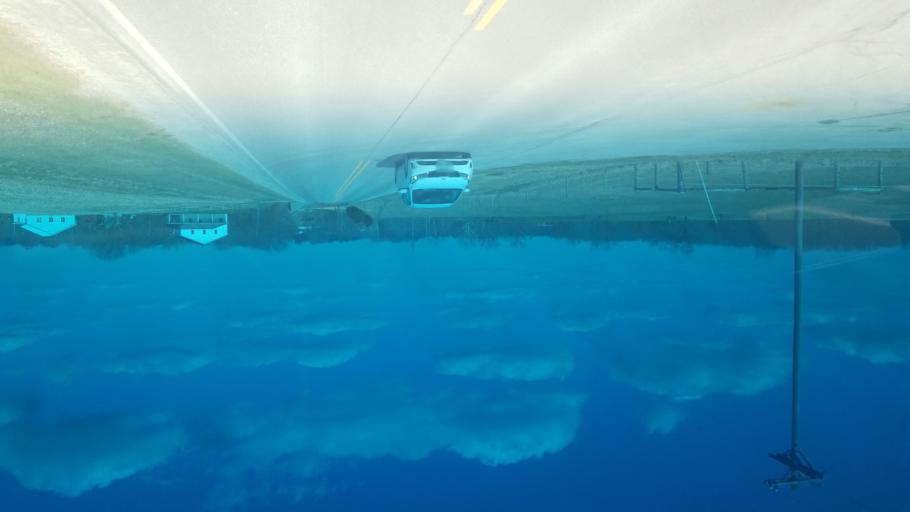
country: US
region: Ohio
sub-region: Highland County
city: Greenfield
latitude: 39.3060
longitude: -83.4384
